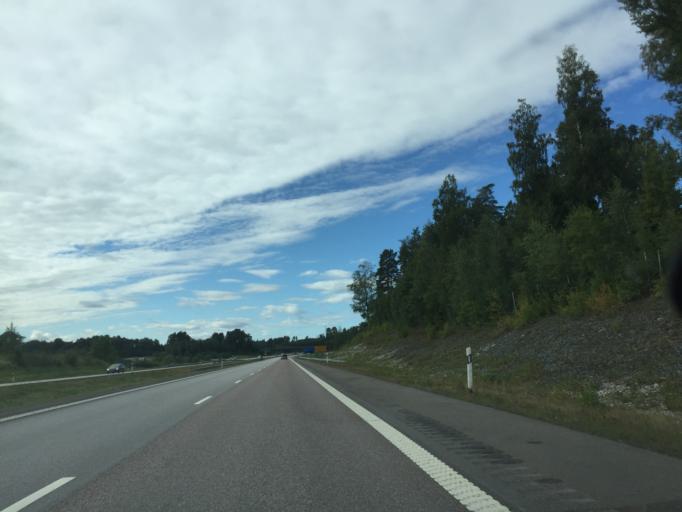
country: SE
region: OErebro
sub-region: Lindesbergs Kommun
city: Frovi
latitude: 59.3118
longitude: 15.4240
